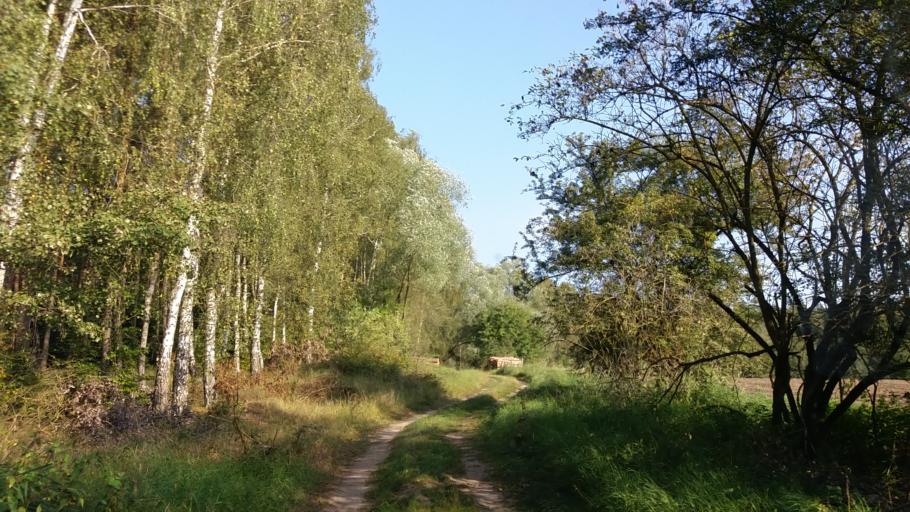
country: PL
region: West Pomeranian Voivodeship
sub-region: Powiat choszczenski
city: Recz
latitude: 53.1909
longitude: 15.5413
